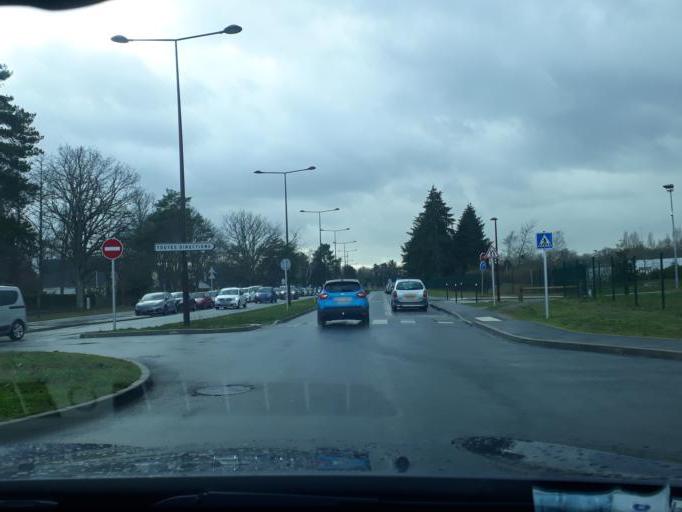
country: FR
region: Centre
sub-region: Departement du Loiret
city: Olivet
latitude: 47.8342
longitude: 1.9218
